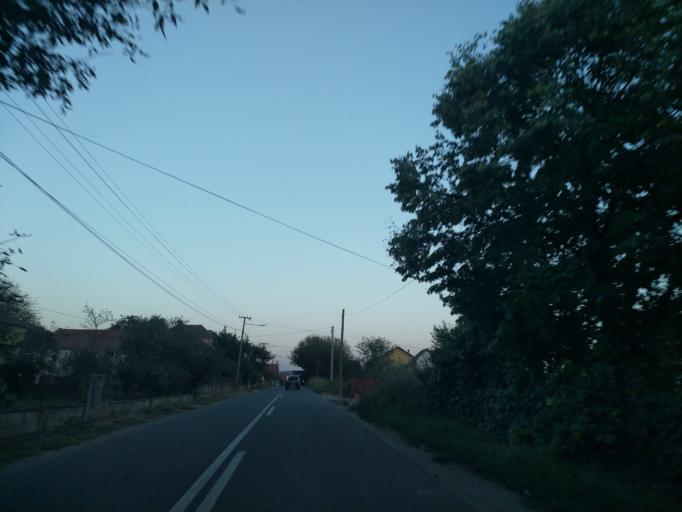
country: RS
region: Central Serbia
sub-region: Rasinski Okrug
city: Krusevac
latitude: 43.6256
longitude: 21.3405
